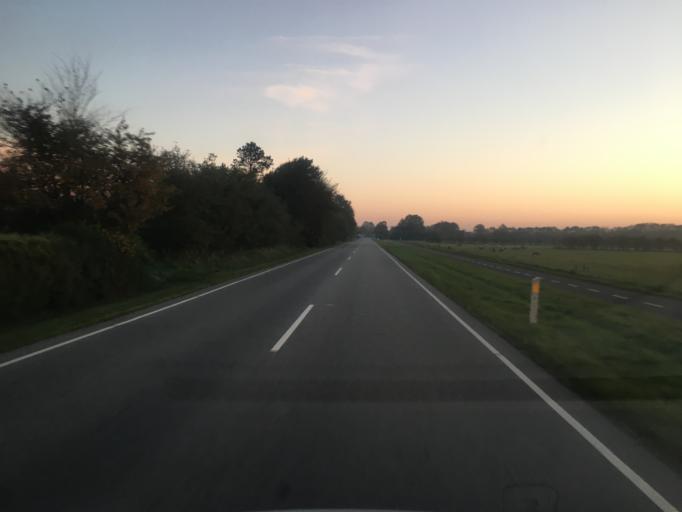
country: DE
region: Schleswig-Holstein
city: Bramstedtlund
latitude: 54.9332
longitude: 9.0725
